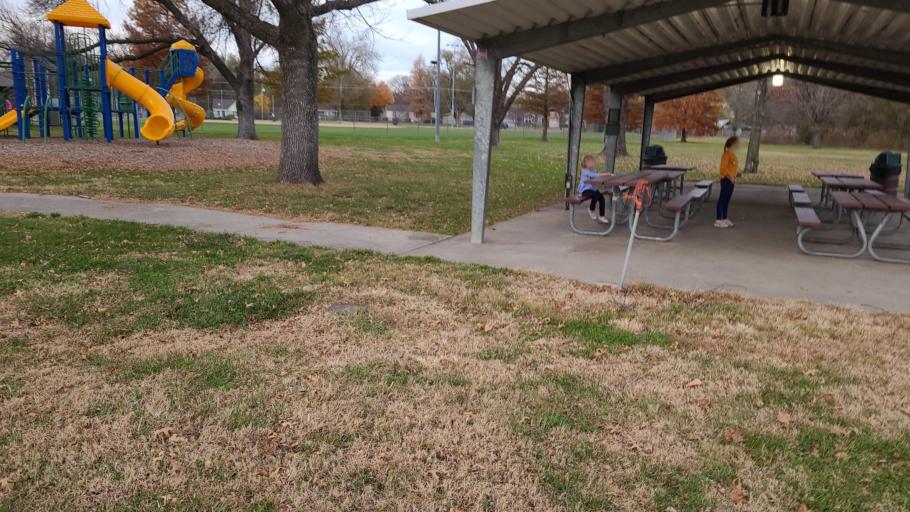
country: US
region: Kansas
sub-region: Douglas County
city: Lawrence
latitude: 38.9807
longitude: -95.2222
